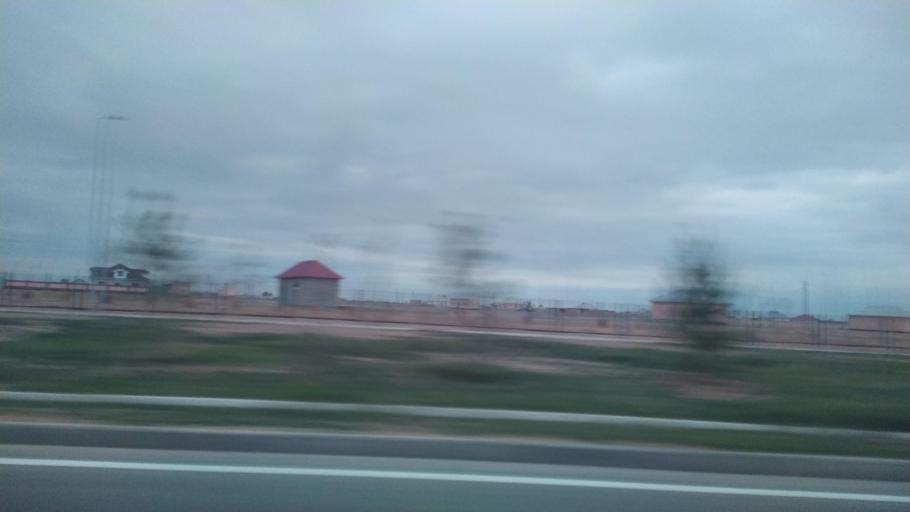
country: KZ
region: Ongtustik Qazaqstan
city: Turkestan
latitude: 43.2753
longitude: 68.4117
